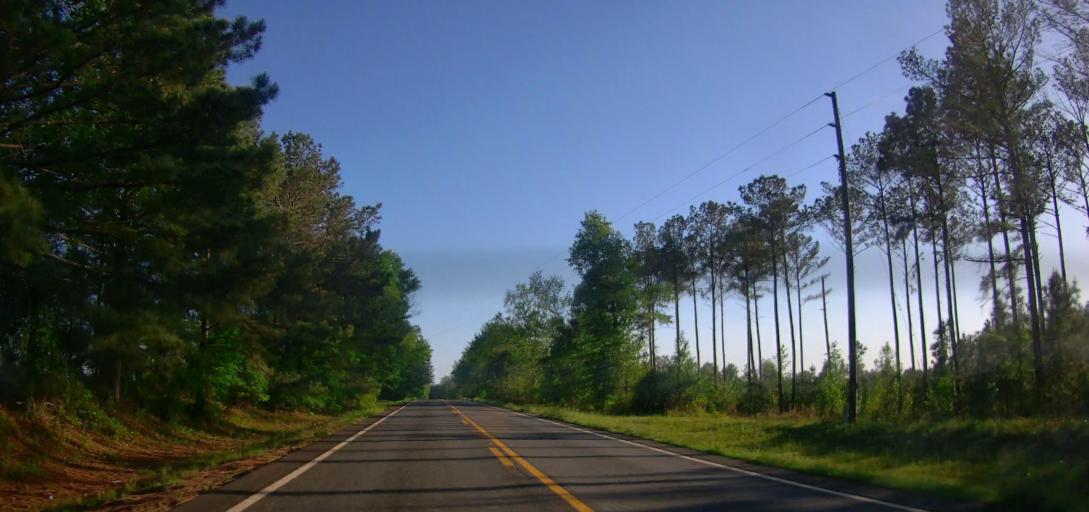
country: US
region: Georgia
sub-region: Macon County
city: Oglethorpe
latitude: 32.2920
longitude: -84.1561
